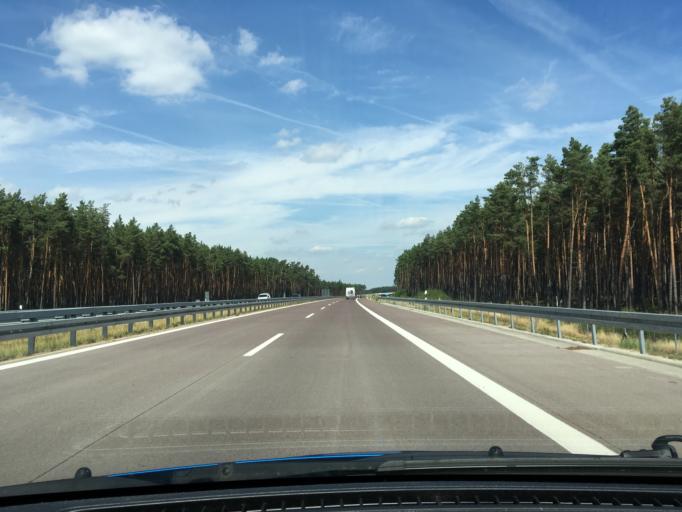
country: DE
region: Mecklenburg-Vorpommern
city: Ludwigslust
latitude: 53.3495
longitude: 11.5173
